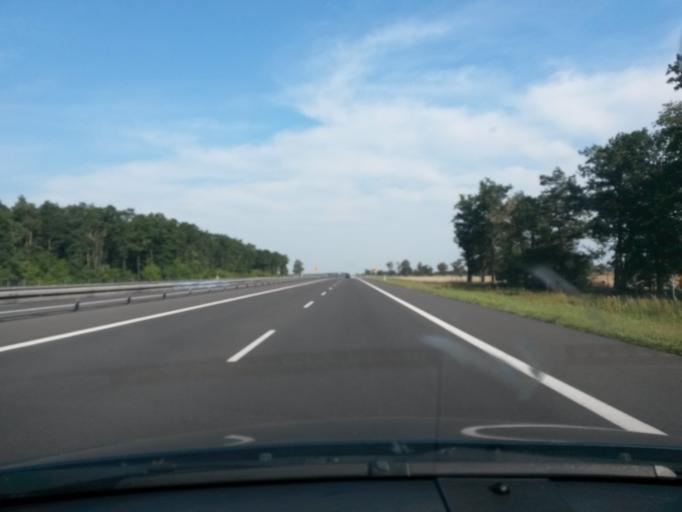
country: PL
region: Greater Poland Voivodeship
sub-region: Powiat wrzesinski
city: Wrzesnia
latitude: 52.3049
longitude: 17.6069
